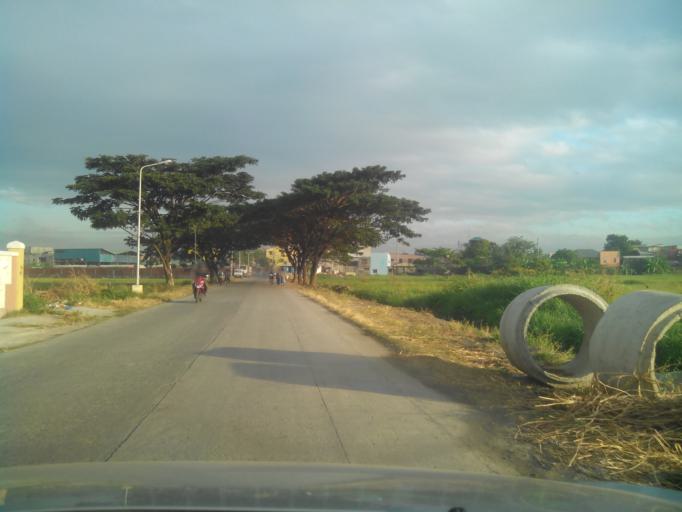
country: PH
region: Calabarzon
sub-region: Province of Rizal
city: Taytay
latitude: 14.5631
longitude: 121.1235
